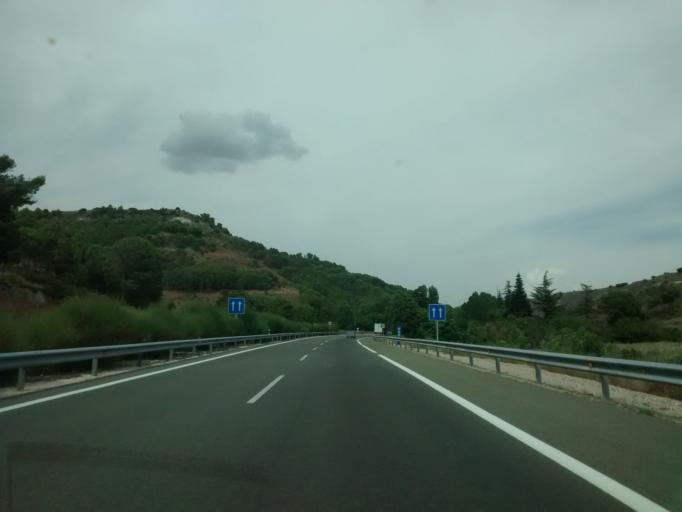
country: ES
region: Castille-La Mancha
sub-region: Provincia de Guadalajara
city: Torija
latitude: 40.7241
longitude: -3.0554
